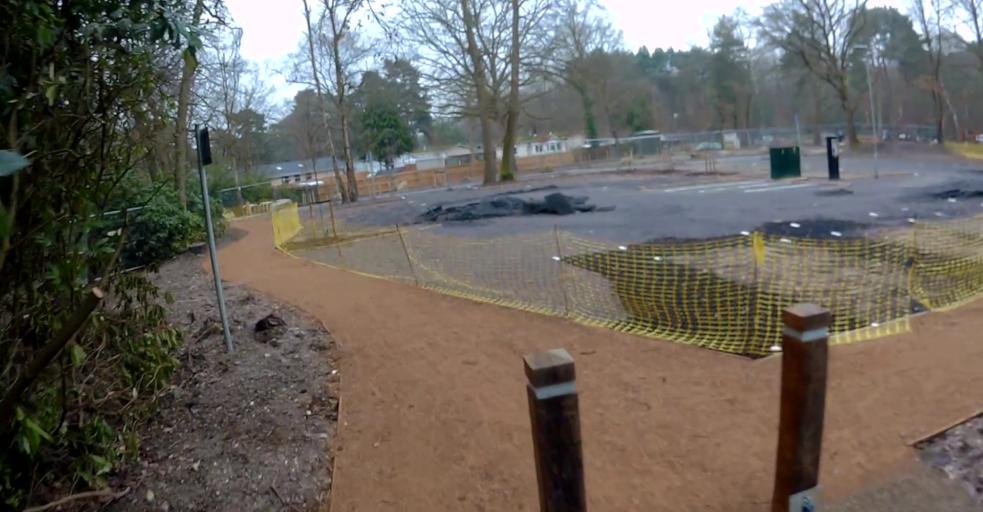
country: GB
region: England
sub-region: Wokingham
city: Barkham
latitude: 51.3785
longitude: -0.8731
